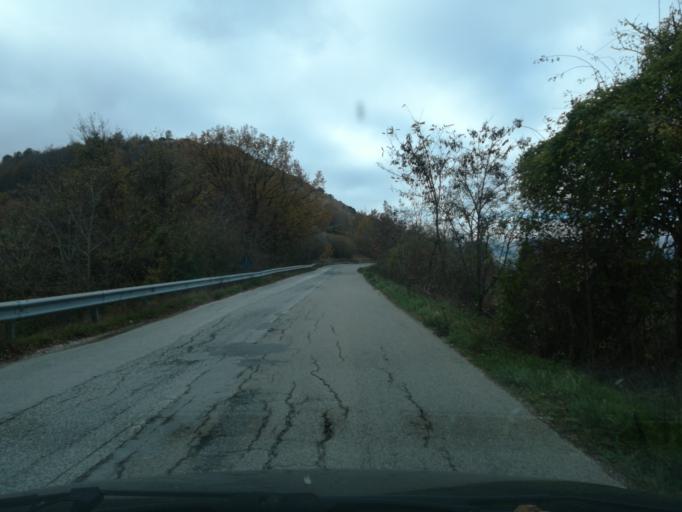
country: IT
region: Molise
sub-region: Provincia di Isernia
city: Agnone
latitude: 41.8255
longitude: 14.3813
